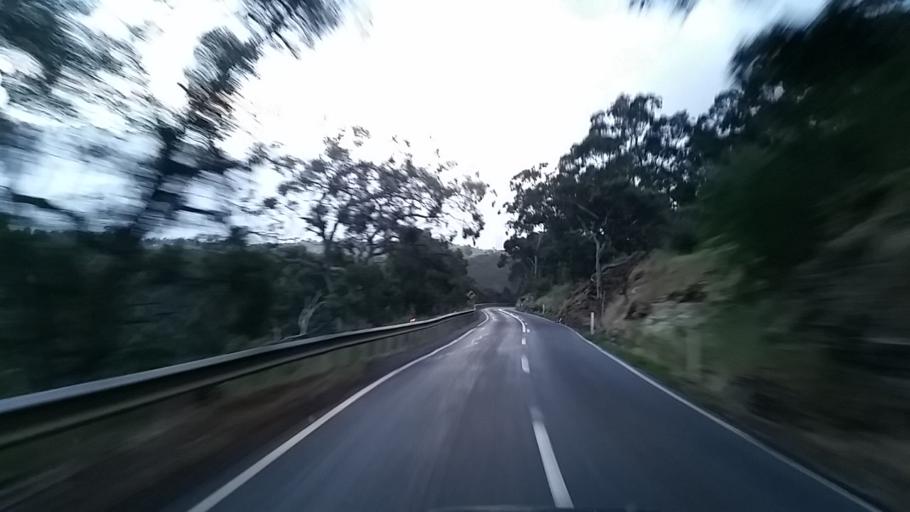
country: AU
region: South Australia
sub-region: Burnside
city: Beaumont
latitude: -34.9518
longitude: 138.6864
